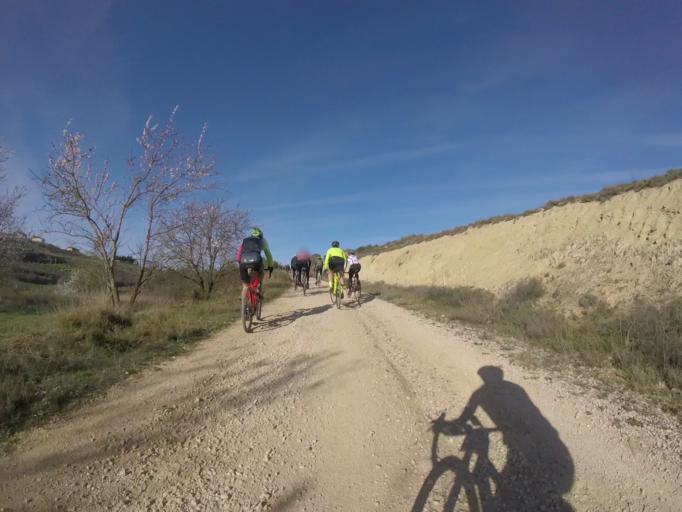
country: ES
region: Navarre
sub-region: Provincia de Navarra
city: Yerri
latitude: 42.6876
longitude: -1.9546
